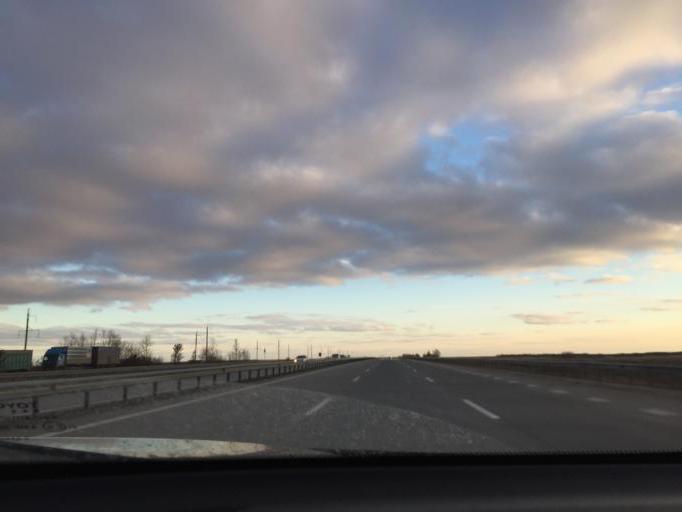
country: KZ
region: Astana Qalasy
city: Astana
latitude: 51.3532
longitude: 71.3355
